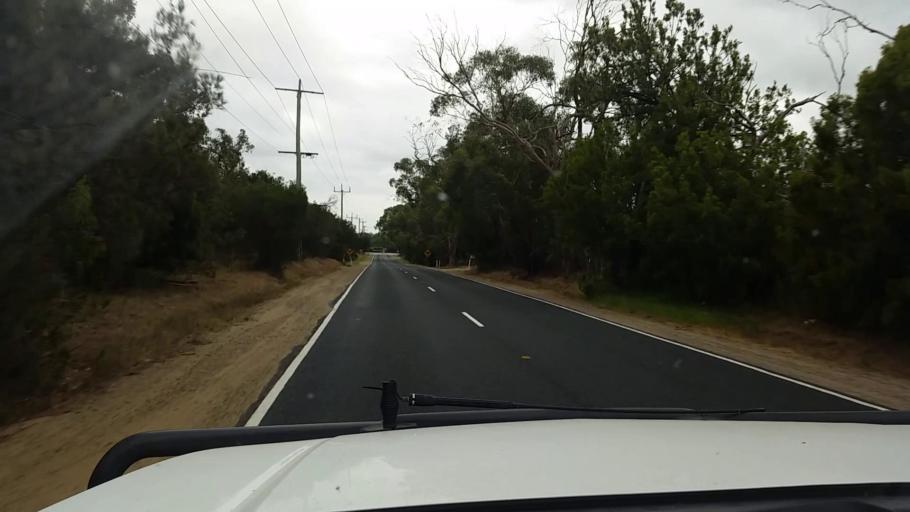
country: AU
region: Victoria
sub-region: Mornington Peninsula
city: Baxter
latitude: -38.2078
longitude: 145.1581
